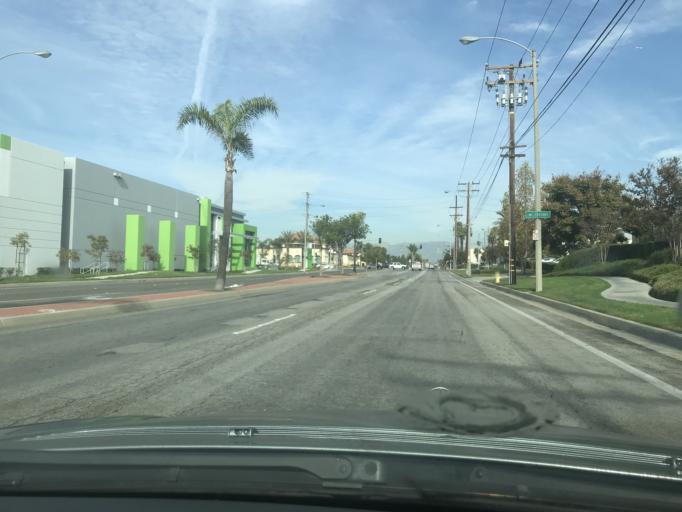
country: US
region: California
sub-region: Los Angeles County
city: Santa Fe Springs
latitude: 33.9339
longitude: -118.0639
